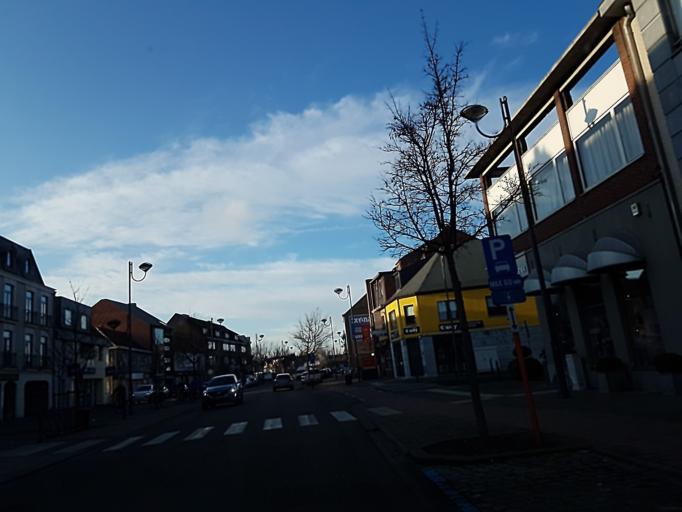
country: BE
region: Flanders
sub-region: Provincie Antwerpen
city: Oud-Turnhout
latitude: 51.3189
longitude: 4.9796
